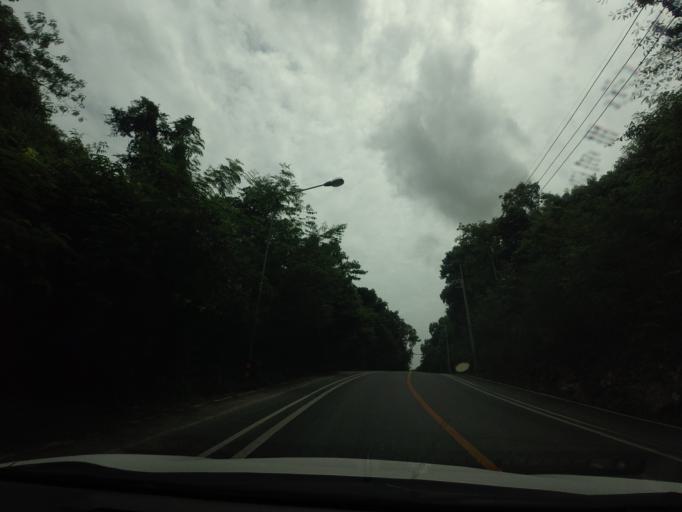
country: TH
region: Rayong
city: Ban Chang
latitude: 12.7620
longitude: 100.9844
